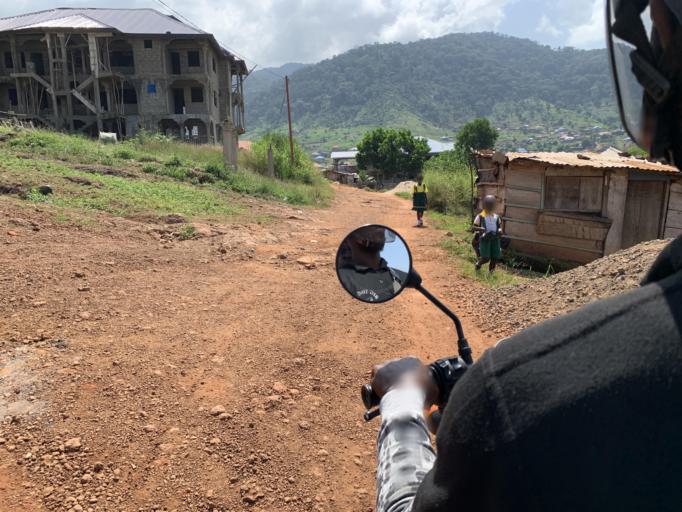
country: SL
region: Western Area
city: Hastings
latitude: 8.3776
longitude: -13.1485
